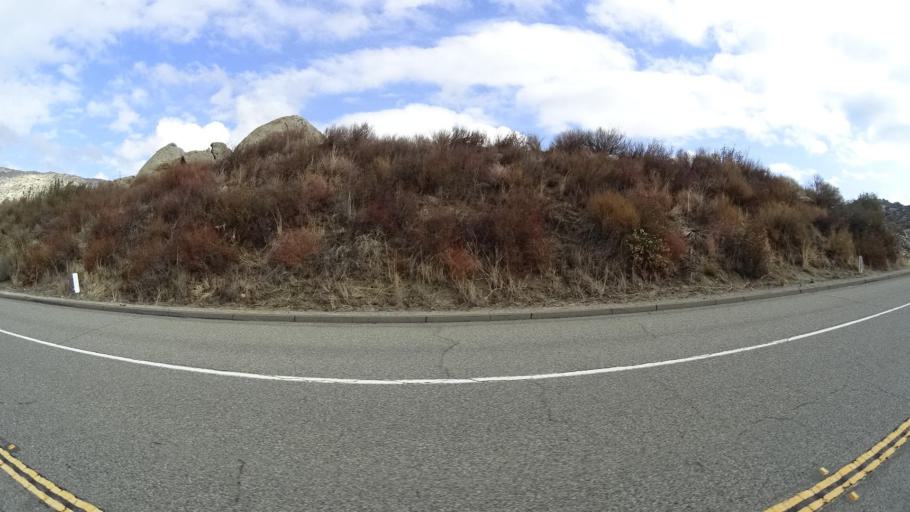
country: MX
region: Baja California
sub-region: Tecate
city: Hacienda Tecate
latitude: 32.5907
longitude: -116.5231
